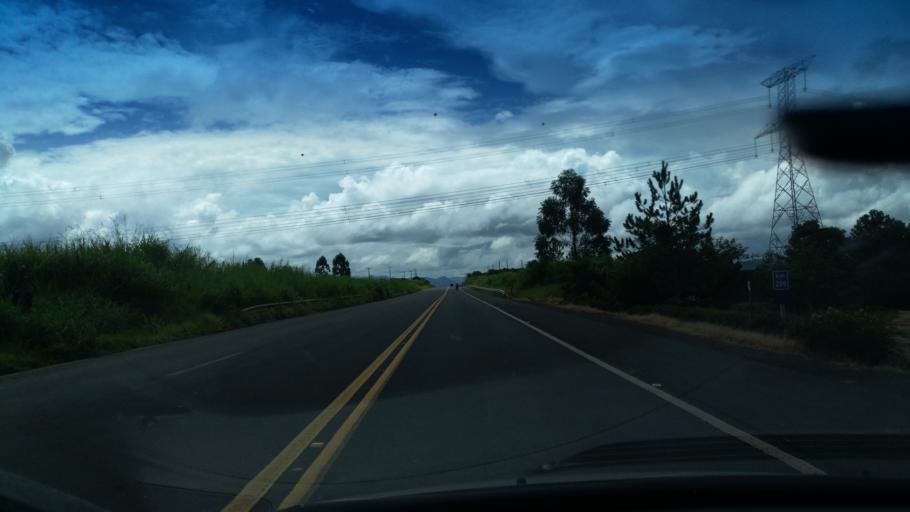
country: BR
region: Sao Paulo
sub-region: Santo Antonio Do Jardim
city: Espirito Santo do Pinhal
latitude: -22.1400
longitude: -46.7090
